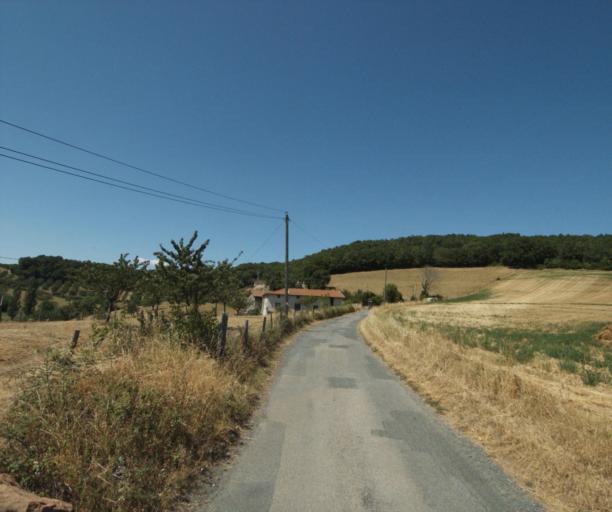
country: FR
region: Rhone-Alpes
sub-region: Departement du Rhone
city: Bessenay
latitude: 45.7804
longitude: 4.5244
